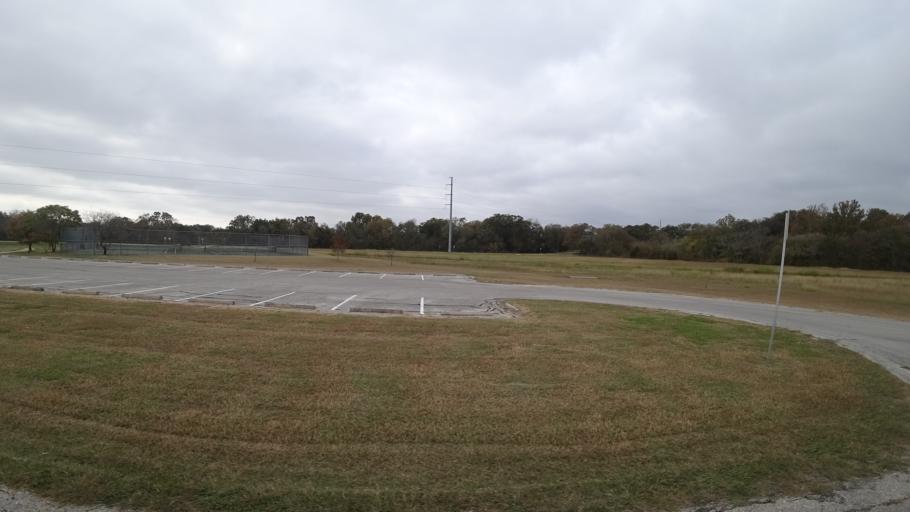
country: US
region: Texas
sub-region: Travis County
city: Pflugerville
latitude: 30.4101
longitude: -97.5987
